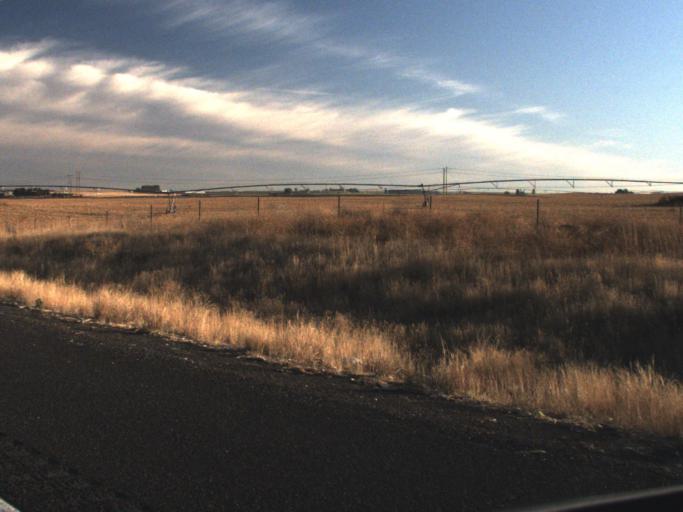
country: US
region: Washington
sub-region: Franklin County
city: Pasco
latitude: 46.3008
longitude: -119.0932
